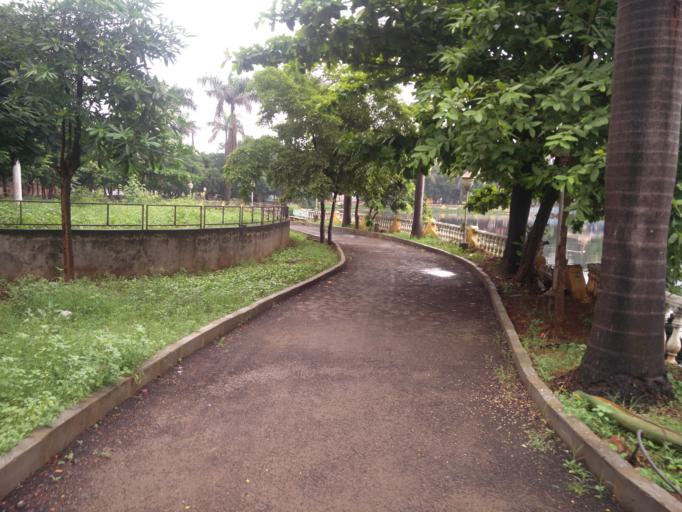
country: IN
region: Andhra Pradesh
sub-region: East Godavari
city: Rajahmundry
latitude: 17.0131
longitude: 81.7785
